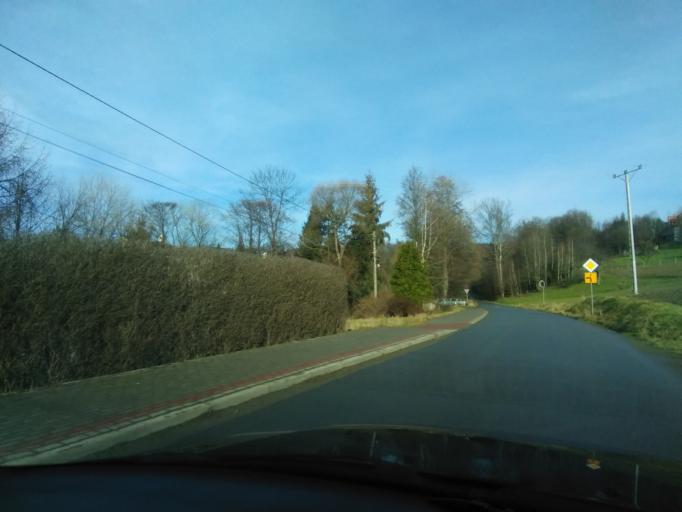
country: PL
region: Subcarpathian Voivodeship
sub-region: Powiat krosnienski
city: Korczyna
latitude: 49.7212
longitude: 21.8074
